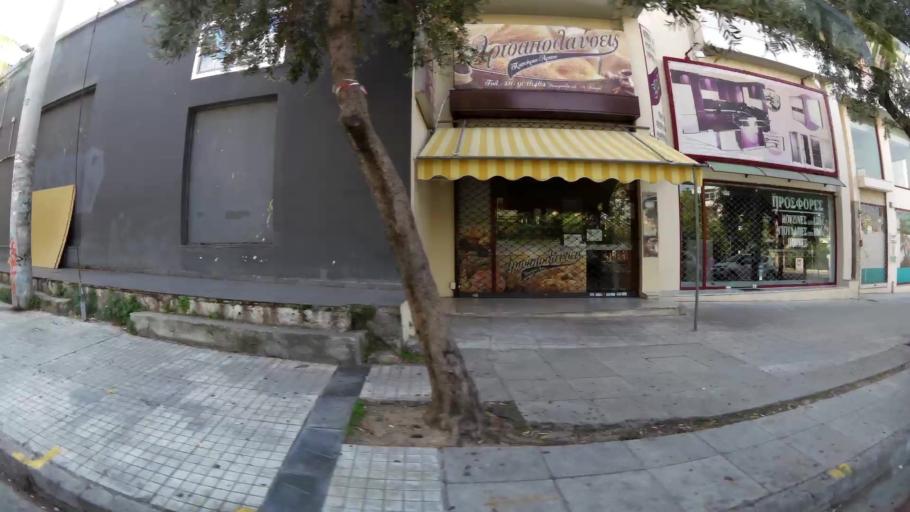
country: GR
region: Attica
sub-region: Nomarchia Athinas
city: Dhafni
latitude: 37.9581
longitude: 23.7252
